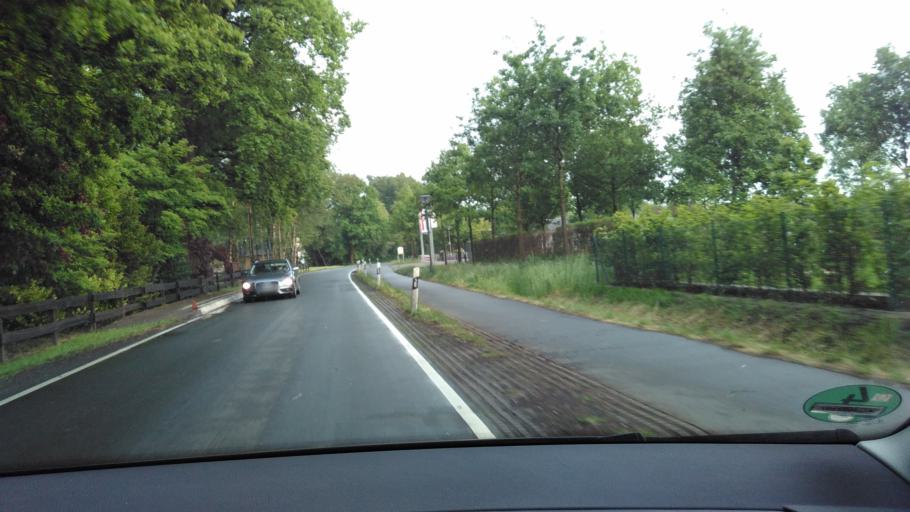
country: DE
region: North Rhine-Westphalia
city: Rietberg
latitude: 51.8222
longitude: 8.4456
